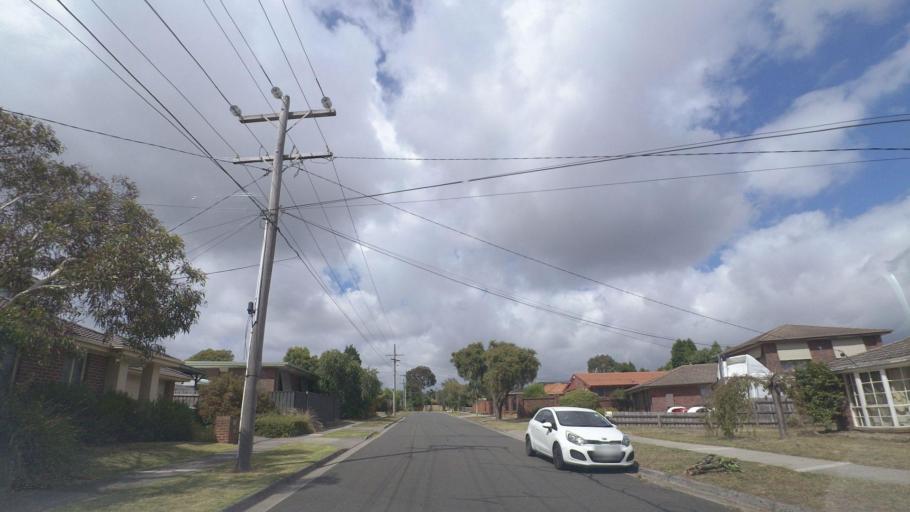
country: AU
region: Victoria
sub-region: Knox
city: Scoresby
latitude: -37.8956
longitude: 145.2288
